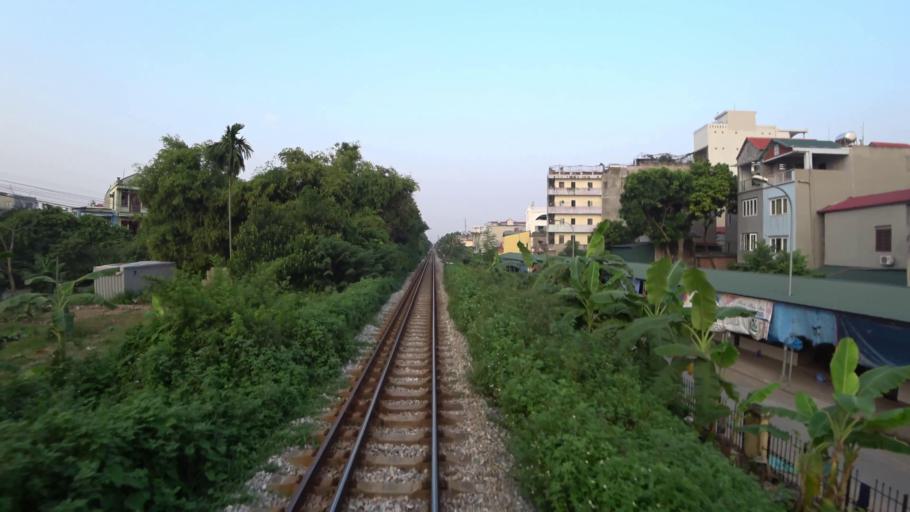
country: VN
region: Ha Noi
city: Trau Quy
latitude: 21.0791
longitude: 105.9100
